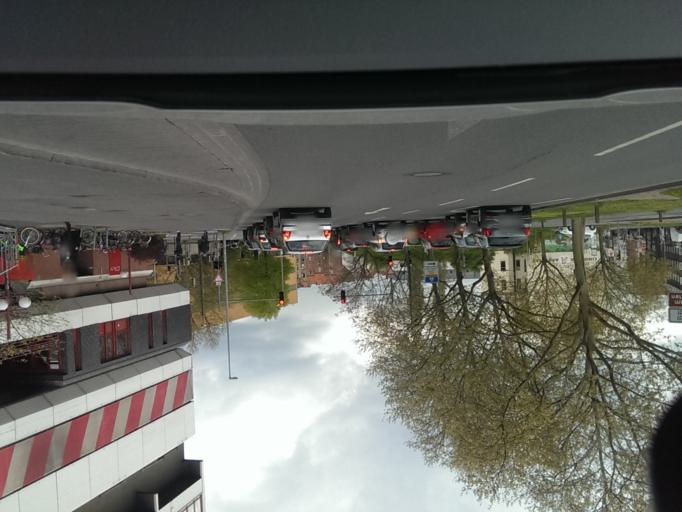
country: DE
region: Lower Saxony
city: Hannover
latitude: 52.3710
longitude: 9.7152
